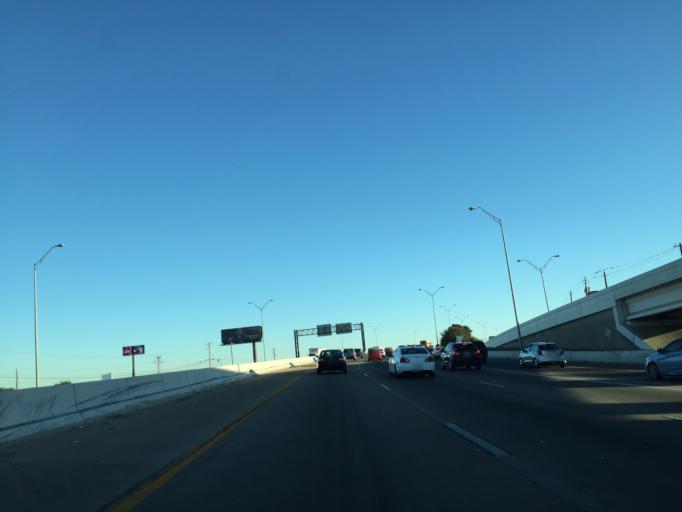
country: US
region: Texas
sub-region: Travis County
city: Wells Branch
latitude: 30.3690
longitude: -97.7194
